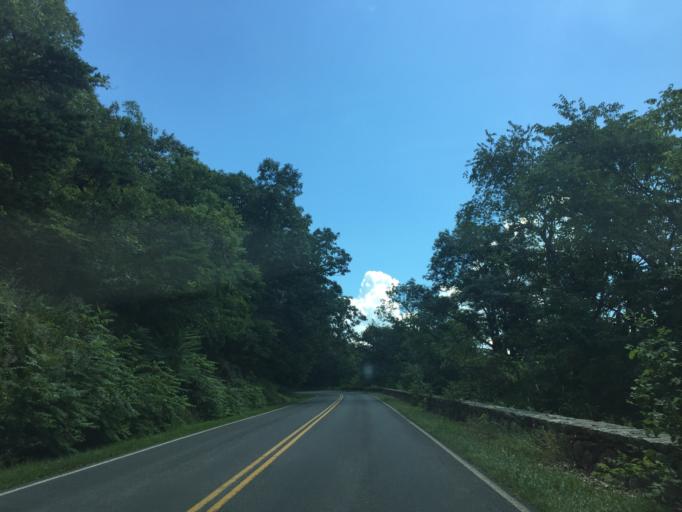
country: US
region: Virginia
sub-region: Warren County
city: Front Royal
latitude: 38.8515
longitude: -78.2065
